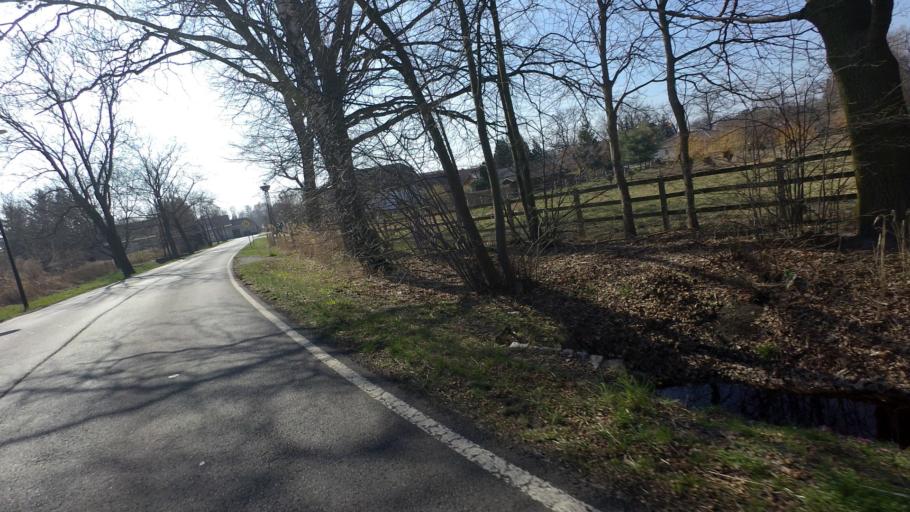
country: DE
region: Brandenburg
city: Sperenberg
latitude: 52.0487
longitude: 13.3209
